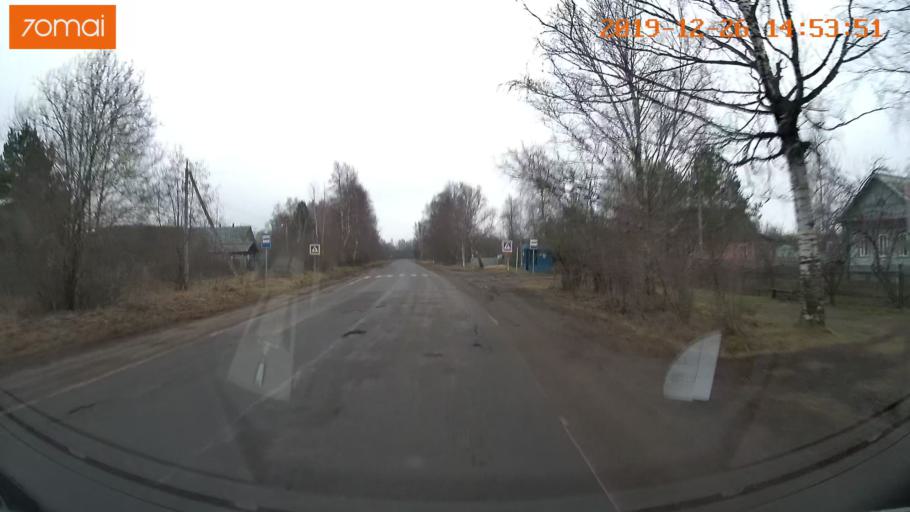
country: RU
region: Jaroslavl
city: Rybinsk
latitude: 58.3120
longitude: 38.8869
